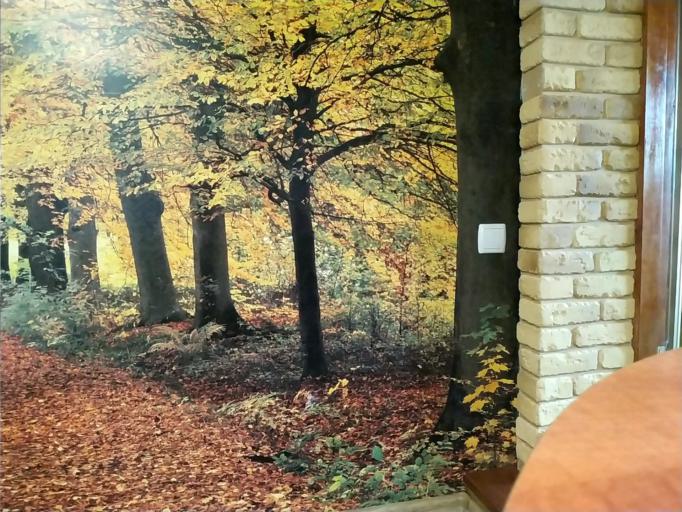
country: RU
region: Leningrad
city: Tolmachevo
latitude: 58.9327
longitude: 29.7081
